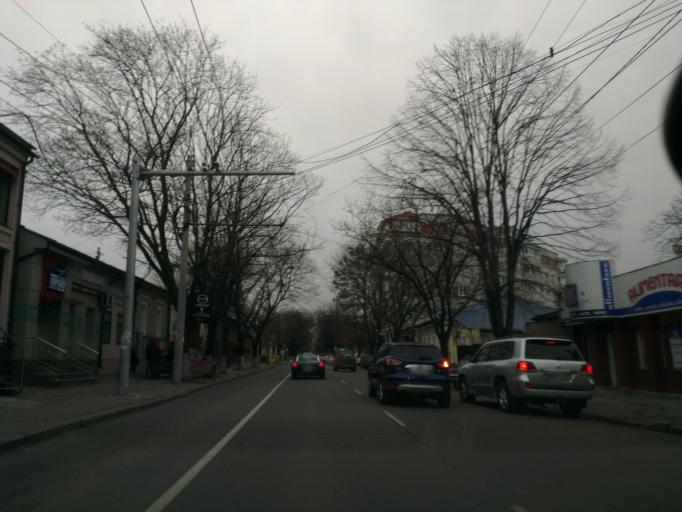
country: MD
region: Chisinau
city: Chisinau
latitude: 47.0179
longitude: 28.8337
